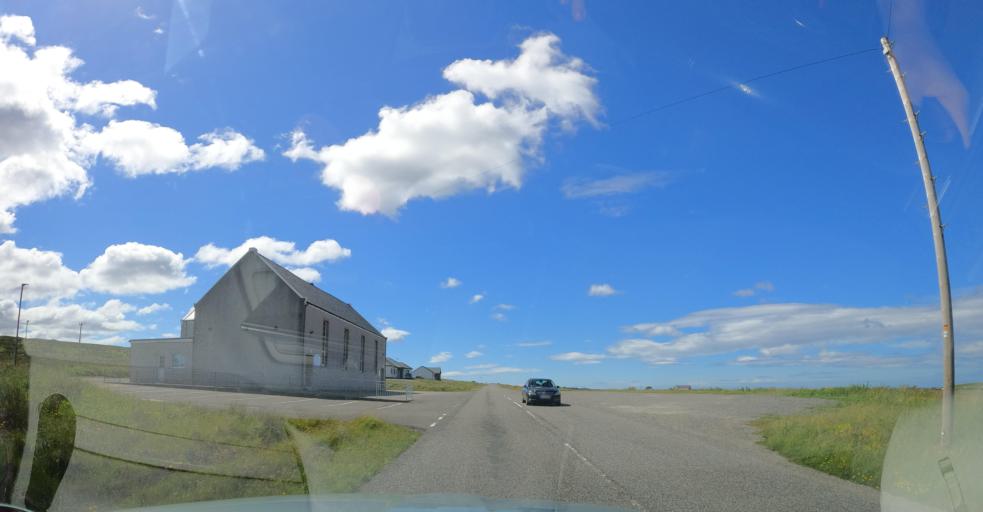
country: GB
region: Scotland
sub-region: Eilean Siar
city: Isle of Lewis
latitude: 58.3487
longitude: -6.5252
